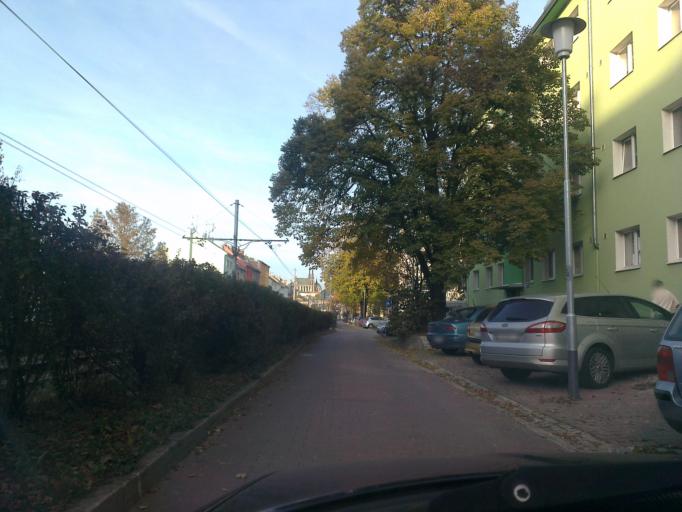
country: CZ
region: South Moravian
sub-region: Mesto Brno
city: Brno
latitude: 49.1804
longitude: 16.5990
